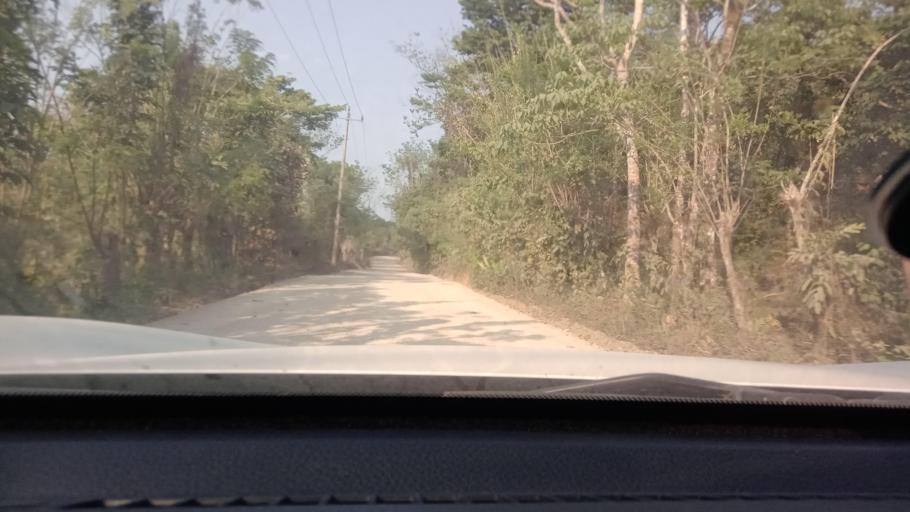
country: MX
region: Tabasco
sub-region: Huimanguillo
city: Francisco Rueda
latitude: 17.6559
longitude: -93.8720
